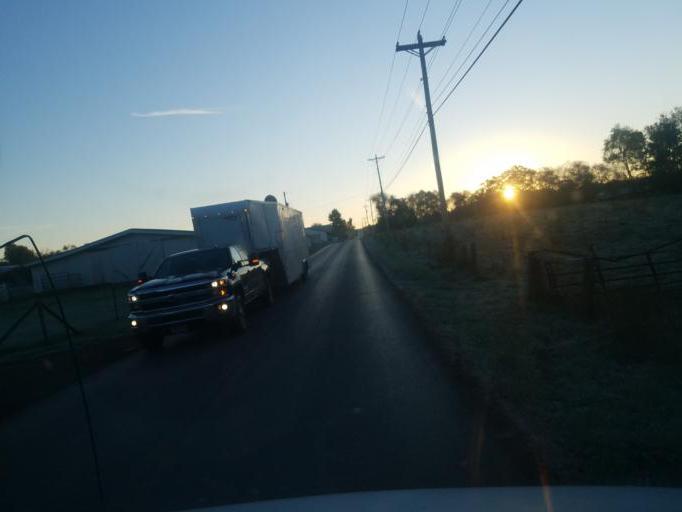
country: US
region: Ohio
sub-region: Stark County
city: Brewster
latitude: 40.6533
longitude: -81.6995
